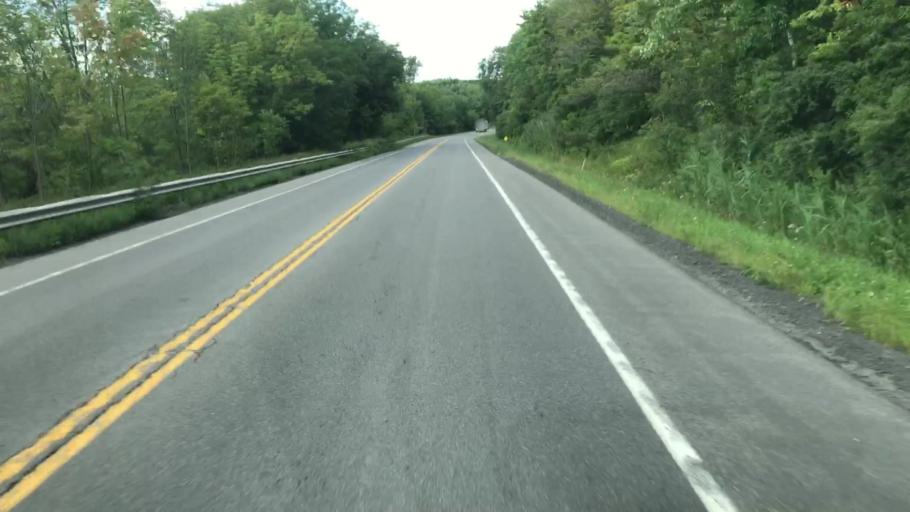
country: US
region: New York
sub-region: Onondaga County
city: Marcellus
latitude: 42.9677
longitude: -76.3367
